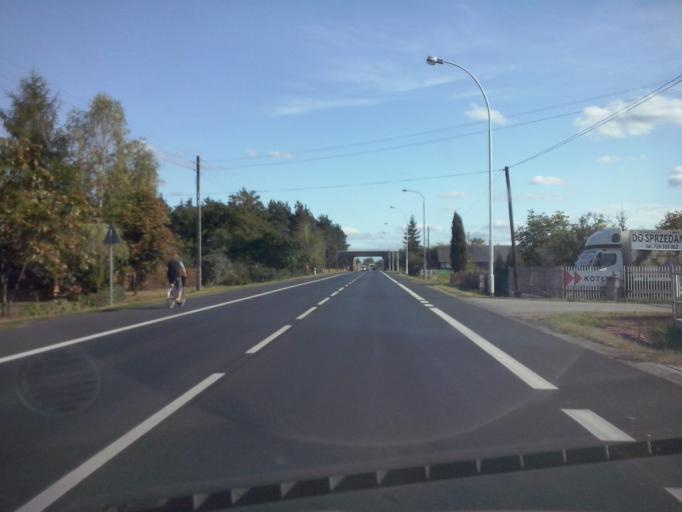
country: PL
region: Subcarpathian Voivodeship
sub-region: Powiat nizanski
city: Nisko
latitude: 50.5329
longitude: 22.1056
